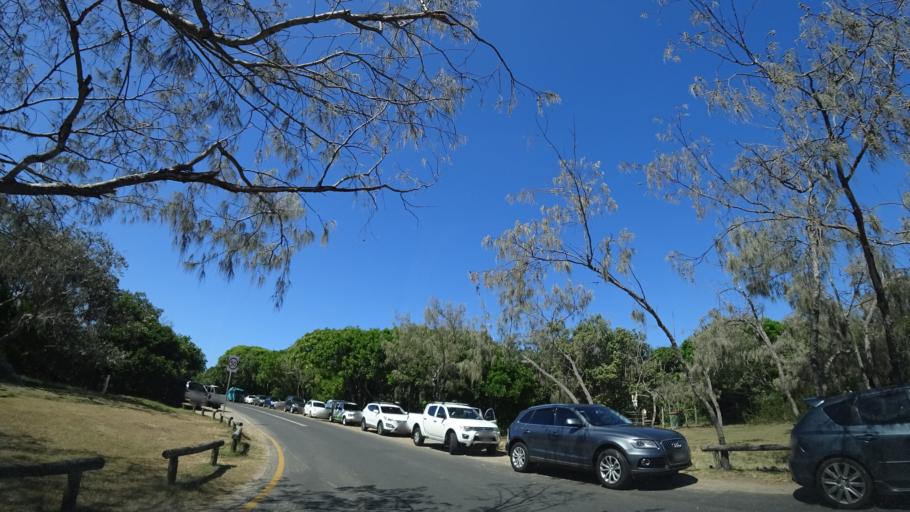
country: AU
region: Queensland
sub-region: Sunshine Coast
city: Mooloolaba
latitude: -26.6388
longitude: 153.1009
